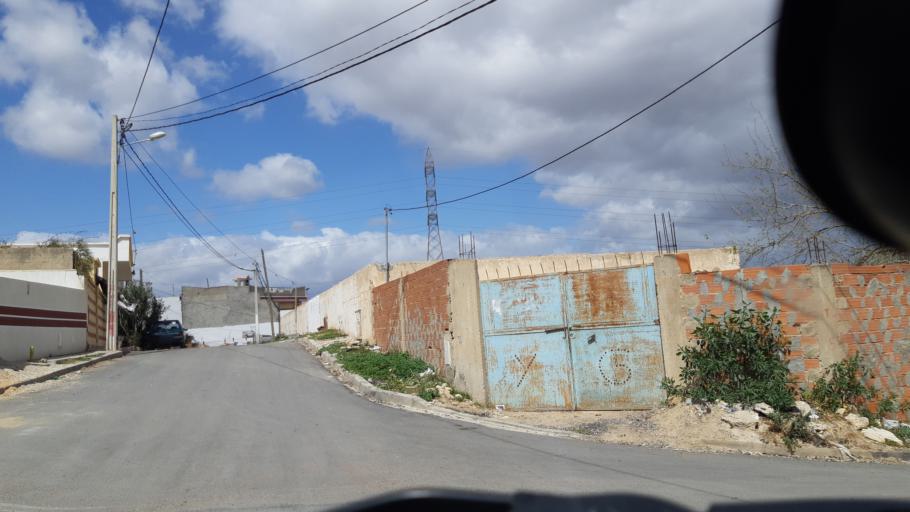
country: TN
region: Susah
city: Akouda
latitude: 35.8783
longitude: 10.5185
